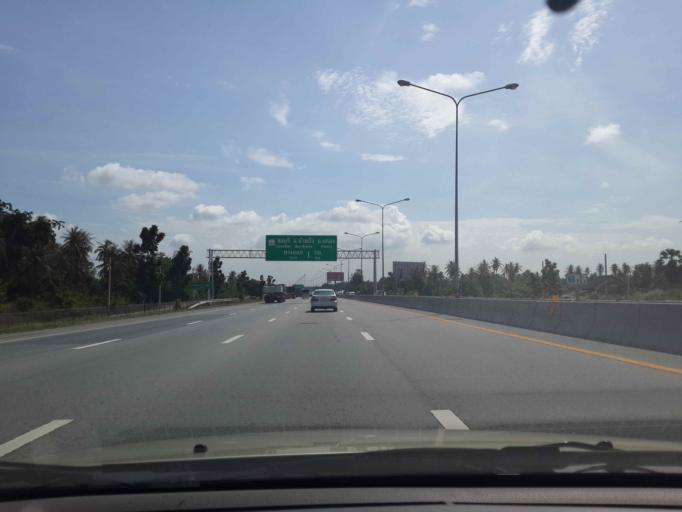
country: TH
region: Chon Buri
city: Chon Buri
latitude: 13.3257
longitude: 101.0158
